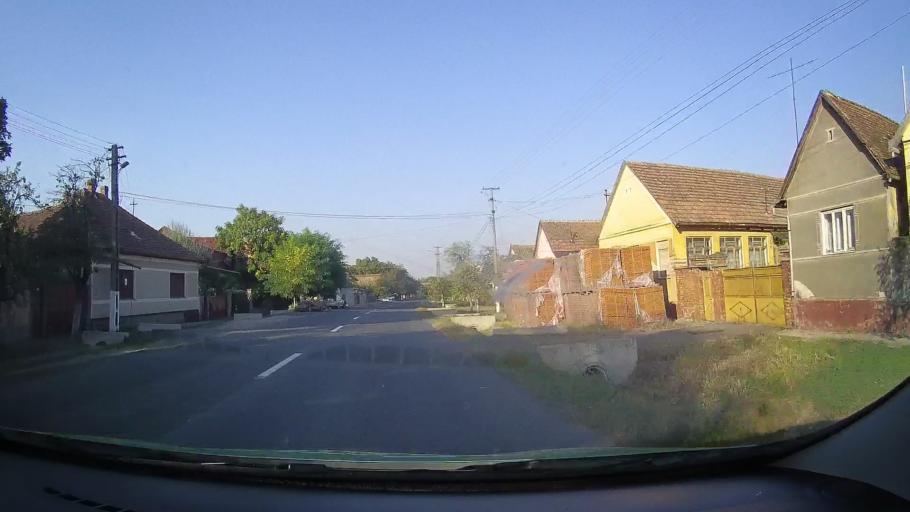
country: RO
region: Arad
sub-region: Comuna Ghioroc
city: Cuvin
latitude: 46.1678
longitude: 21.5942
